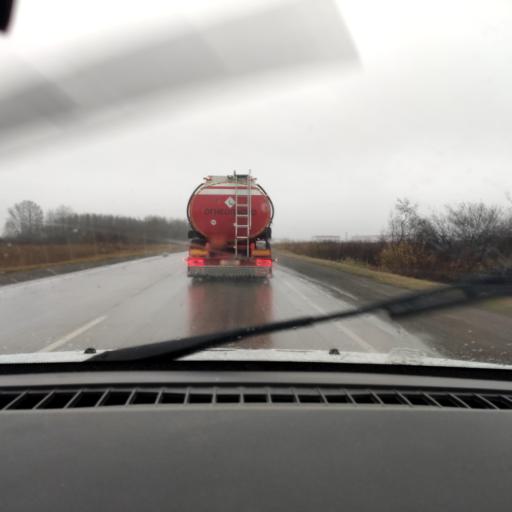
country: RU
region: Perm
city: Froly
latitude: 57.8992
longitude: 56.2312
